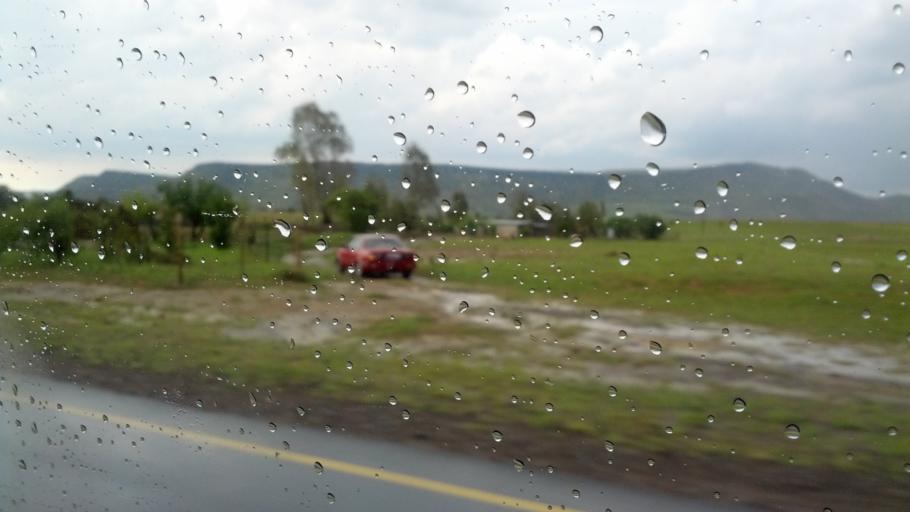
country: LS
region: Mafeteng
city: Mafeteng
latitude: -29.7563
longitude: 27.1206
